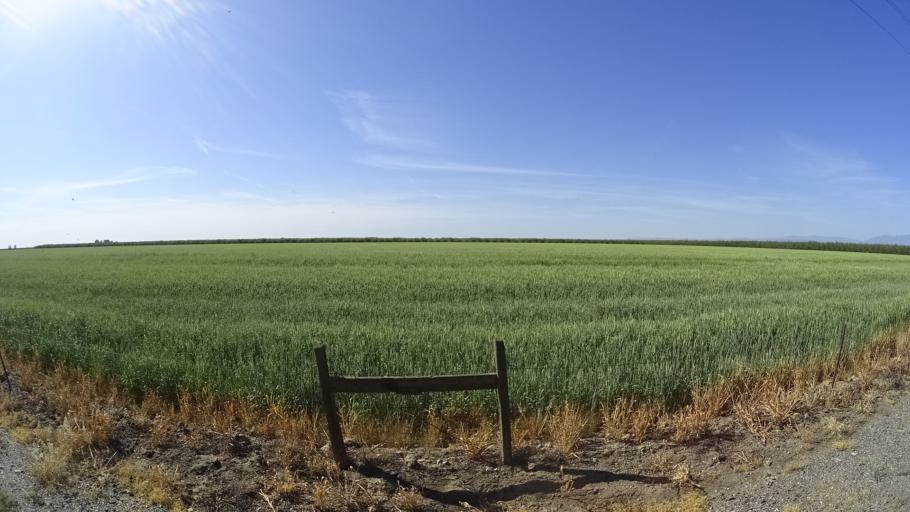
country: US
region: California
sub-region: Glenn County
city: Willows
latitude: 39.6107
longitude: -122.1661
